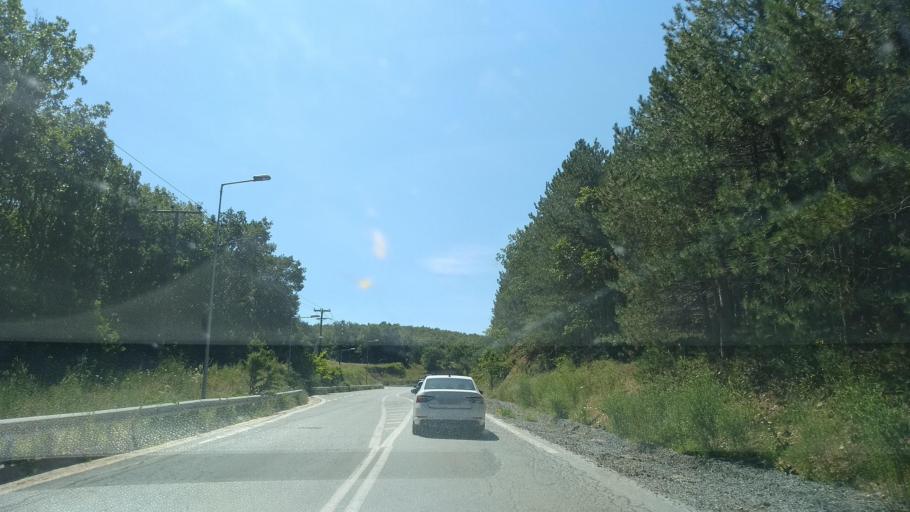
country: GR
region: Central Macedonia
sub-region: Nomos Chalkidikis
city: Megali Panagia
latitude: 40.4588
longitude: 23.6559
